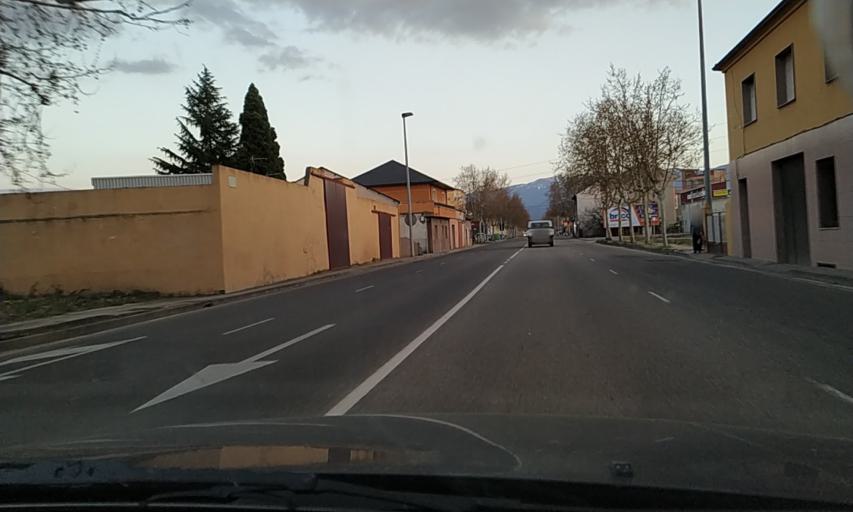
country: ES
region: Castille and Leon
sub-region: Provincia de Leon
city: Ponferrada
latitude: 42.5672
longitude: -6.6063
